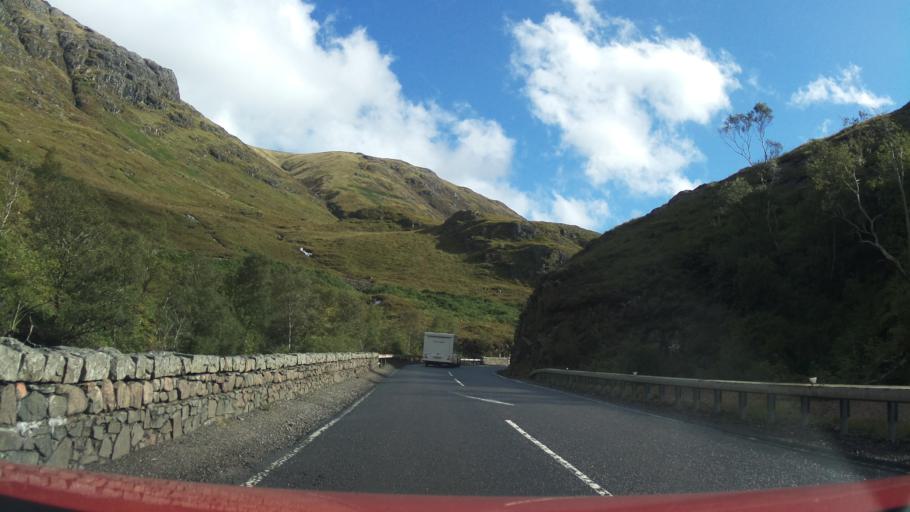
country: GB
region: Scotland
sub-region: Highland
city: Fort William
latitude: 56.6627
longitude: -4.9625
